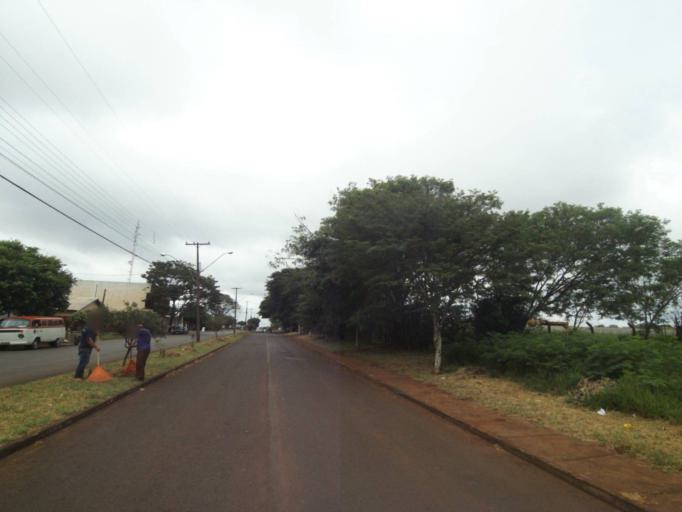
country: BR
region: Parana
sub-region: Campo Mourao
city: Campo Mourao
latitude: -24.0165
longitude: -52.3557
